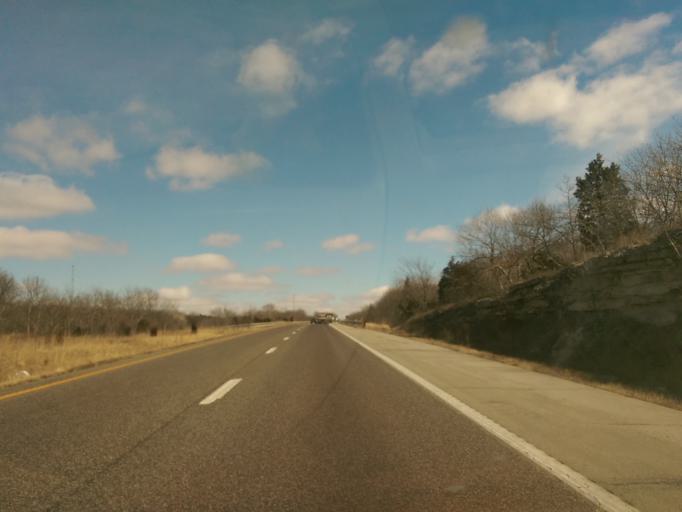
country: US
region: Missouri
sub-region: Montgomery County
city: Montgomery City
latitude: 38.9018
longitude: -91.5712
